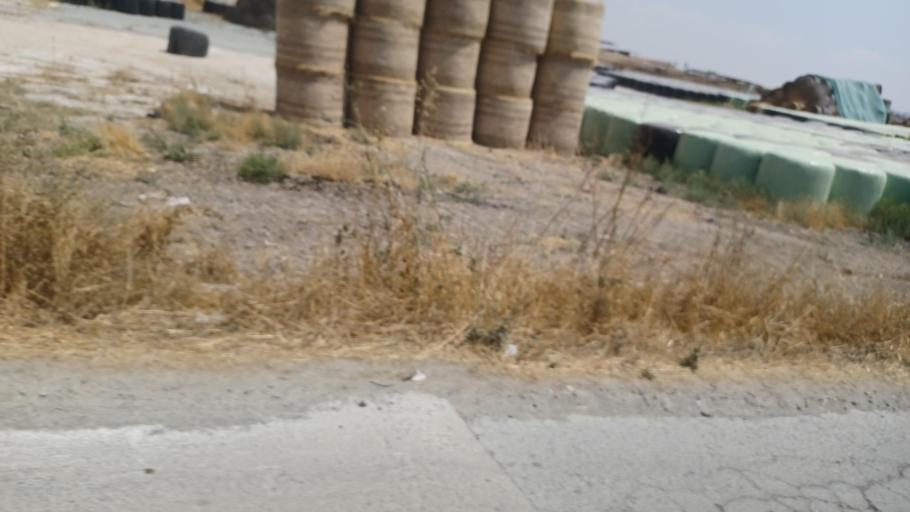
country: CY
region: Larnaka
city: Aradippou
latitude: 34.9633
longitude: 33.5983
